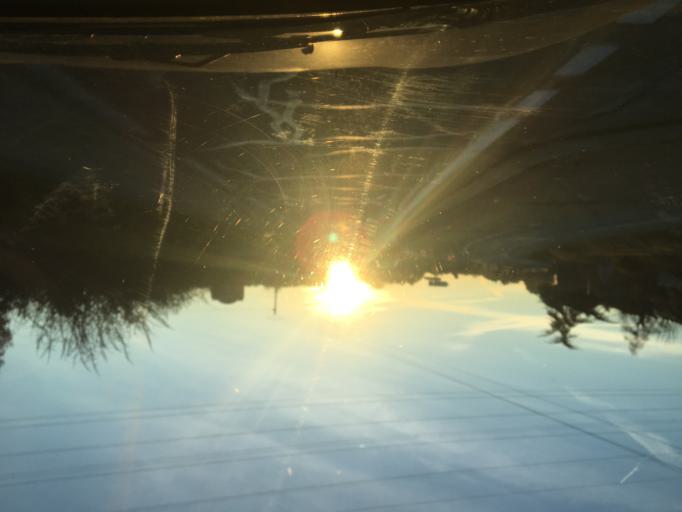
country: FR
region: Provence-Alpes-Cote d'Azur
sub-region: Departement du Var
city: Lorgues
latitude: 43.4670
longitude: 6.3872
